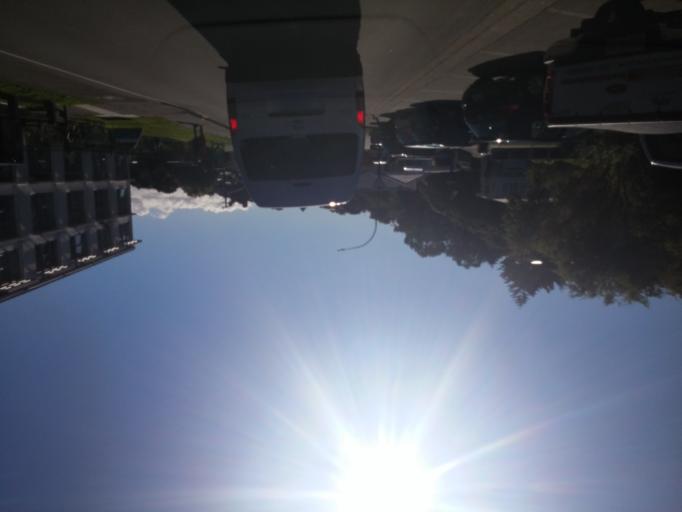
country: NZ
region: Wellington
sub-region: Wellington City
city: Wellington
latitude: -41.2249
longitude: 174.8004
